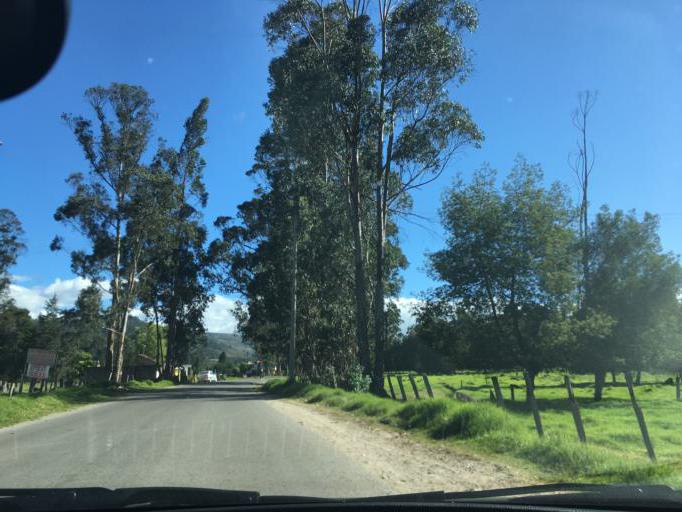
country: CO
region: Boyaca
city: Firavitoba
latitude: 5.6424
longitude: -72.9877
